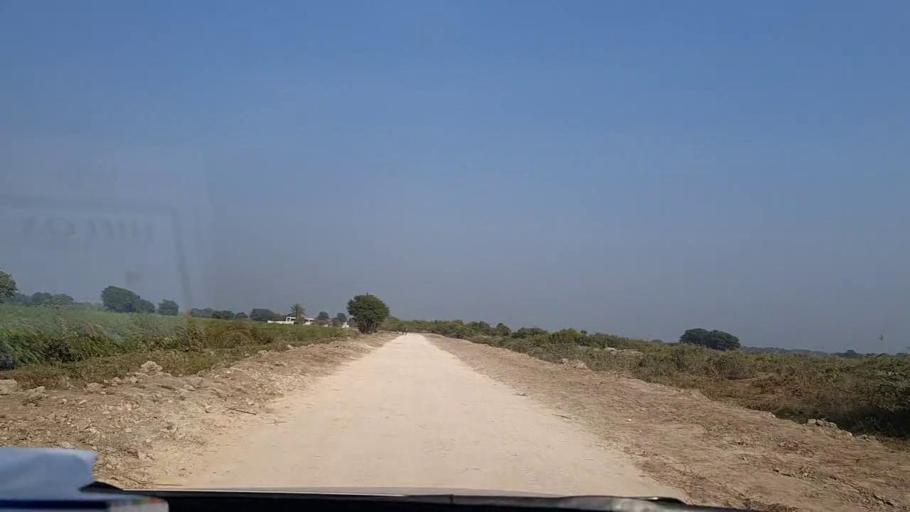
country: PK
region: Sindh
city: Tando Ghulam Ali
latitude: 25.1417
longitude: 68.8729
